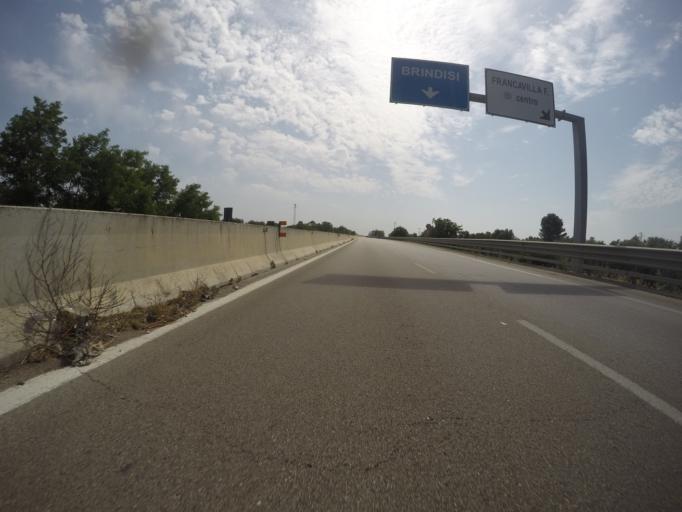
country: IT
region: Apulia
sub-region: Provincia di Brindisi
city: Francavilla Fontana
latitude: 40.5463
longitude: 17.5885
